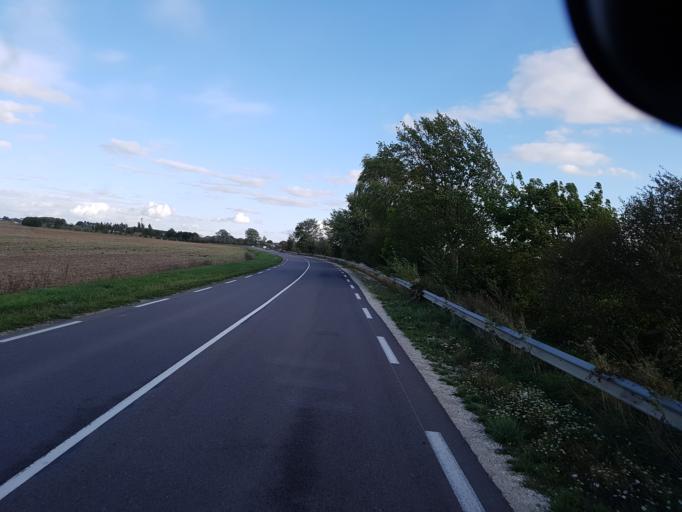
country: FR
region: Ile-de-France
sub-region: Departement de Seine-et-Marne
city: Jouy-le-Chatel
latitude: 48.6894
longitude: 3.0925
